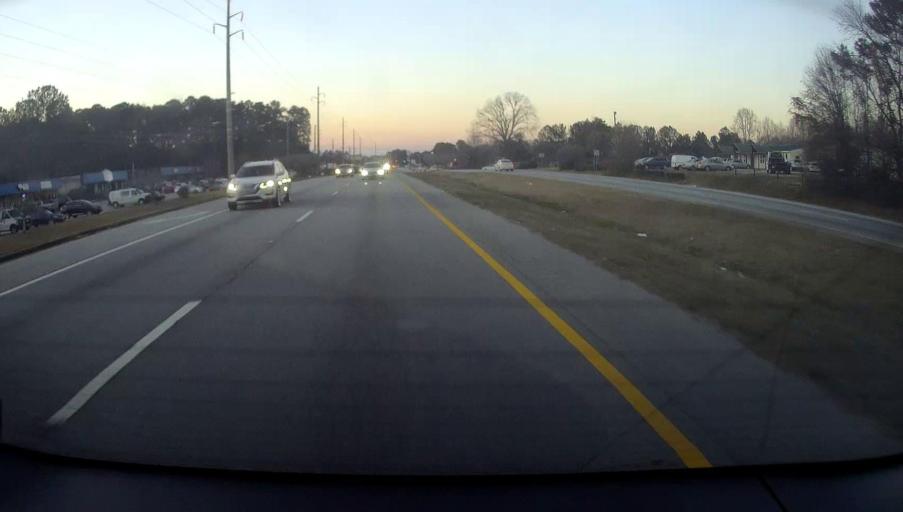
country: US
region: Georgia
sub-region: Fayette County
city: Fayetteville
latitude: 33.5052
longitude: -84.4283
